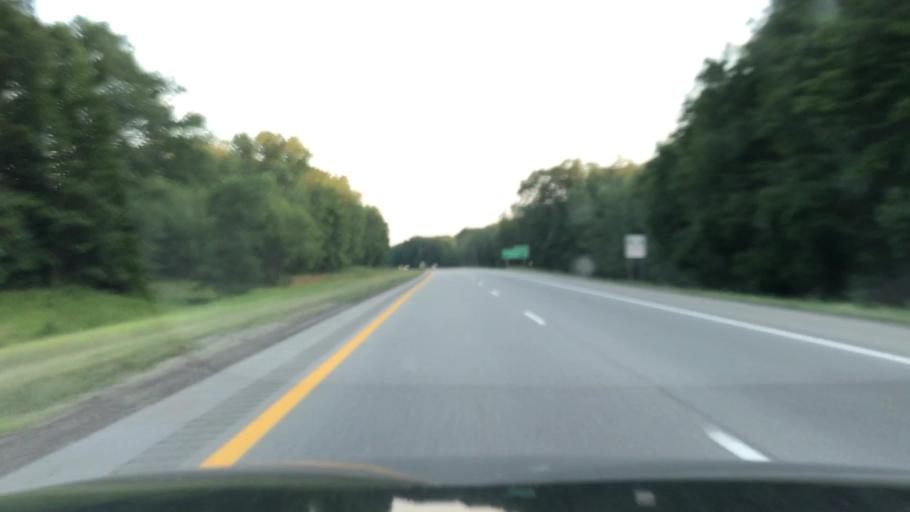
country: US
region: Michigan
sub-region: Montcalm County
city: Howard City
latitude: 43.4986
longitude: -85.4867
